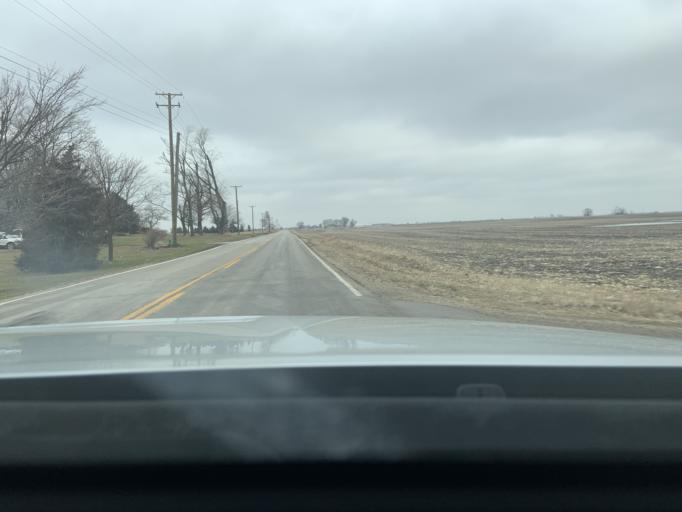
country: US
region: Illinois
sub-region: LaSalle County
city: Seneca
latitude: 41.3403
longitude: -88.6114
